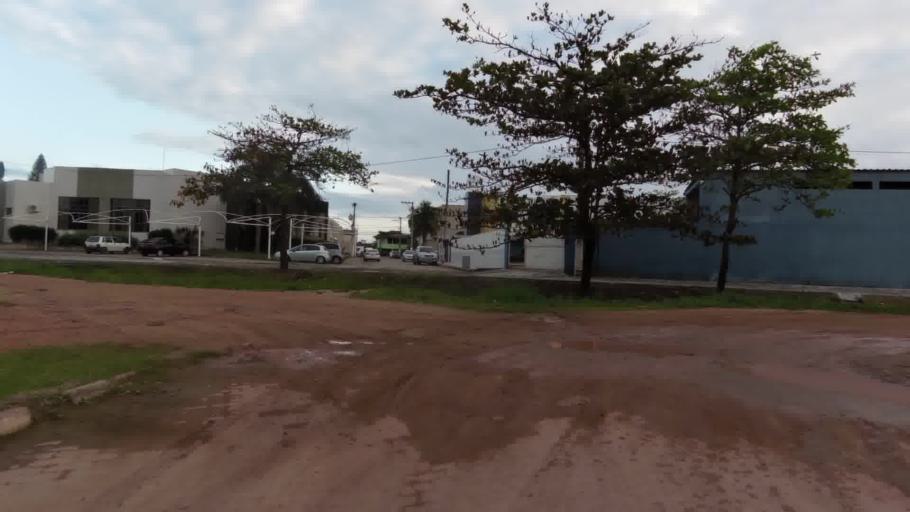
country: BR
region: Espirito Santo
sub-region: Piuma
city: Piuma
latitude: -20.8125
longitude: -40.6313
